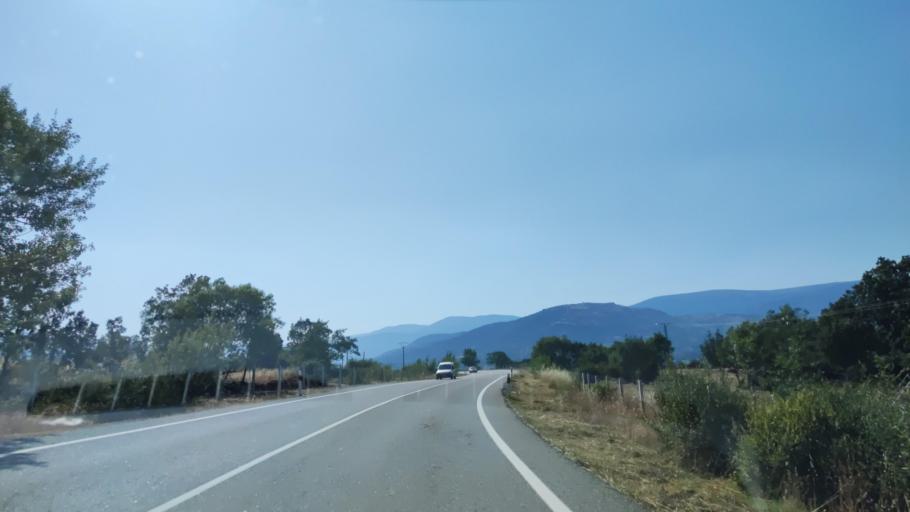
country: ES
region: Madrid
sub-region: Provincia de Madrid
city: Garganta de los Montes
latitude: 40.9435
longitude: -3.6849
